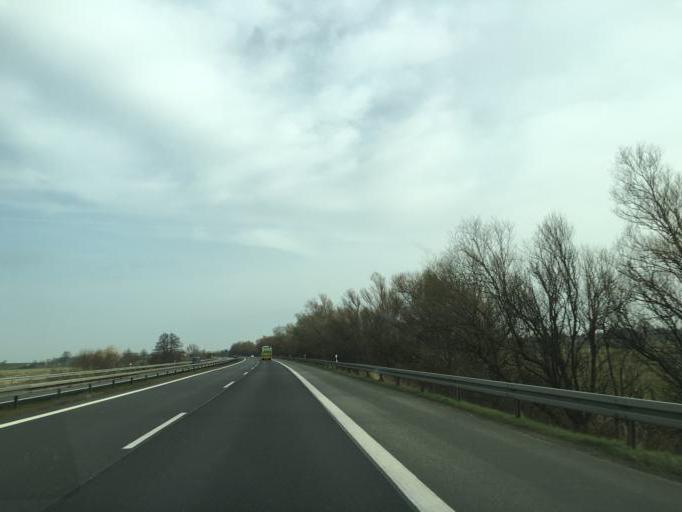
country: DE
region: Brandenburg
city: Fehrbellin
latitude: 52.8300
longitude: 12.7933
